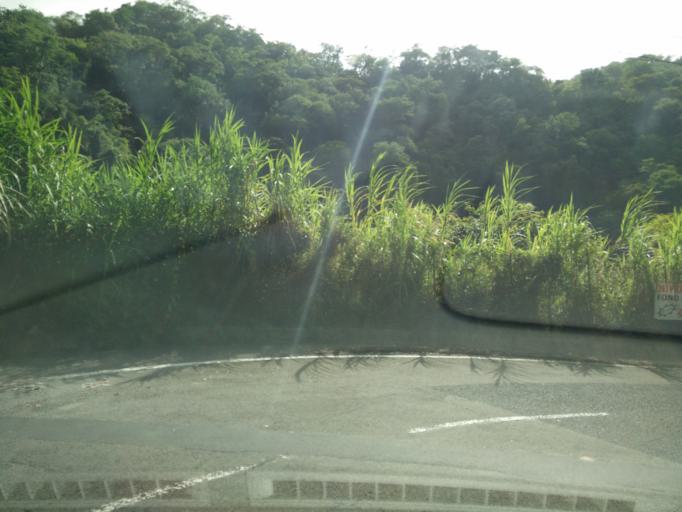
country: MQ
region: Martinique
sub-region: Martinique
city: Basse-Pointe
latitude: 14.8687
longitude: -61.1749
